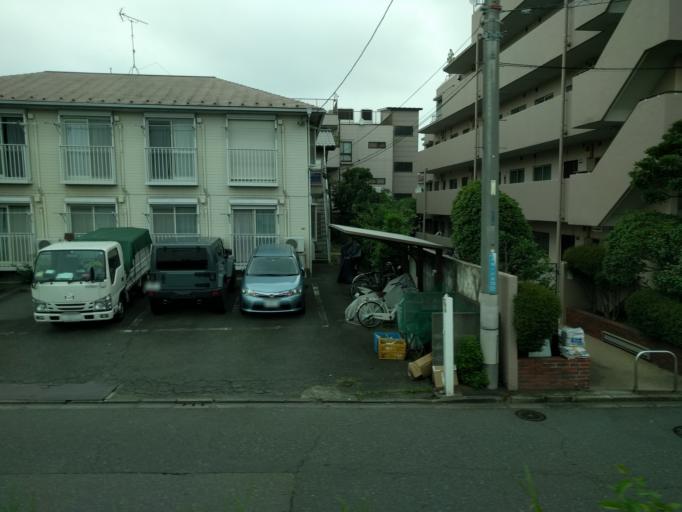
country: JP
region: Kanagawa
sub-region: Kawasaki-shi
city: Kawasaki
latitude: 35.5951
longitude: 139.6512
